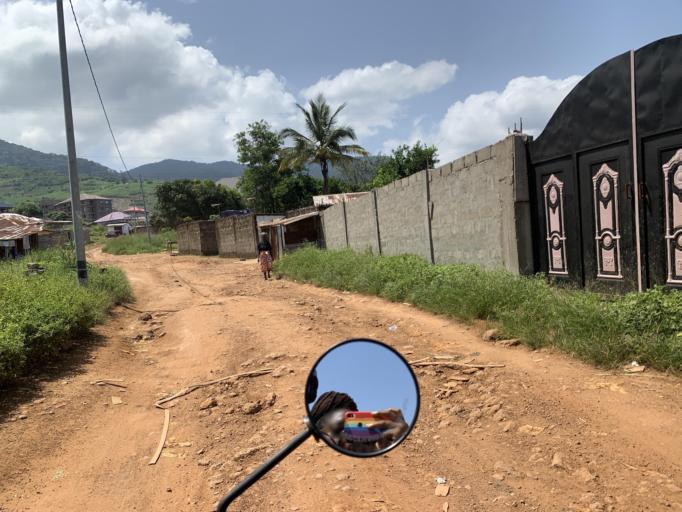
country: SL
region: Western Area
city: Hastings
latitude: 8.3749
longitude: -13.1358
